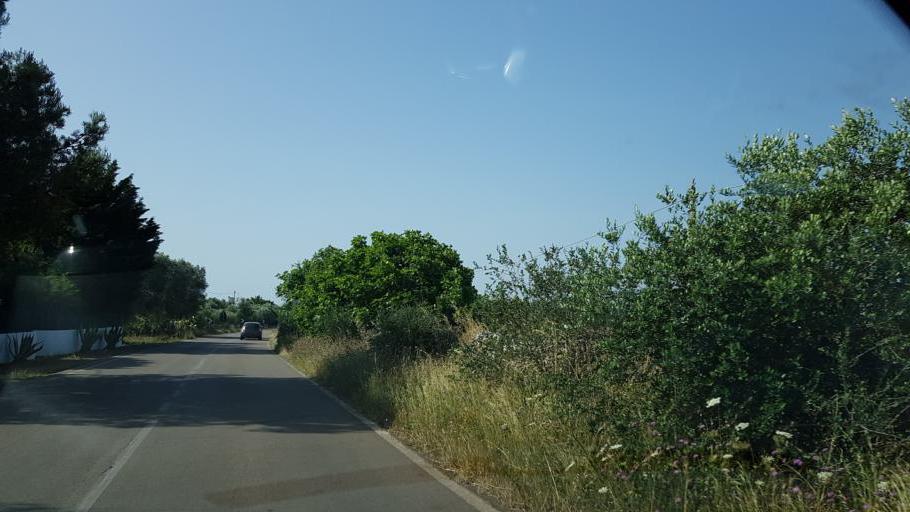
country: IT
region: Apulia
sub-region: Provincia di Lecce
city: Porto Cesareo
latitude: 40.3122
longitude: 17.8628
